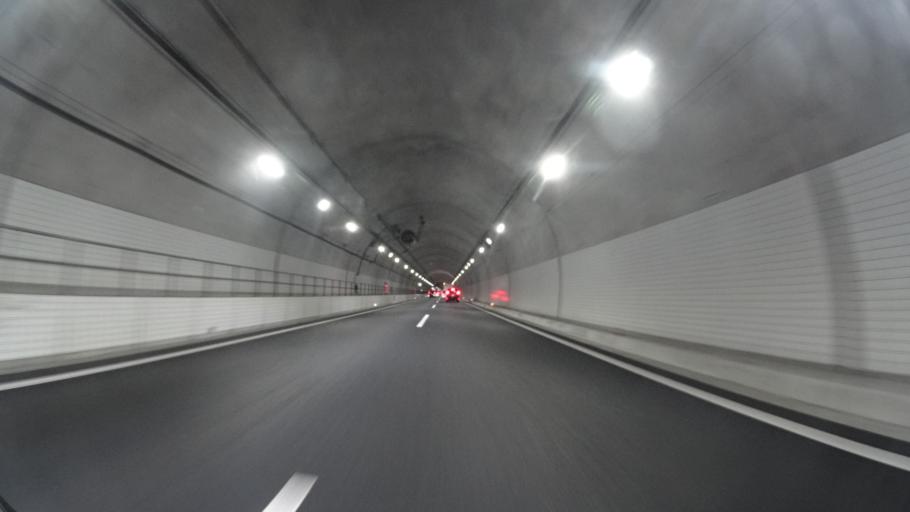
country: JP
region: Mie
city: Komono
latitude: 34.9453
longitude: 136.4480
